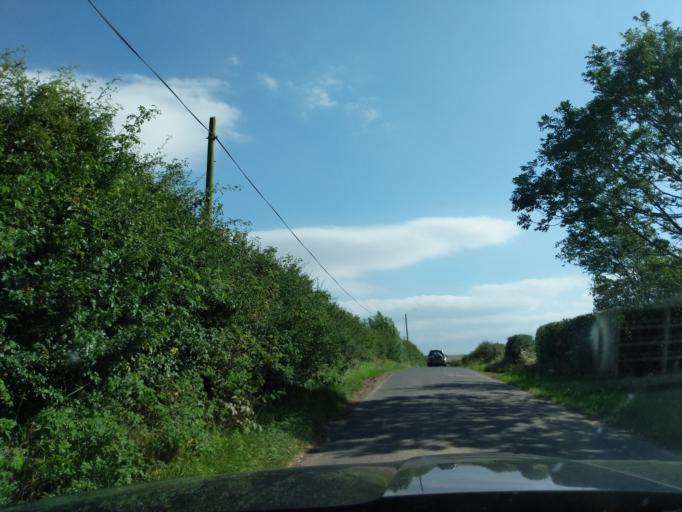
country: GB
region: Scotland
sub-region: The Scottish Borders
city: Coldstream
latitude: 55.6713
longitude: -2.1690
